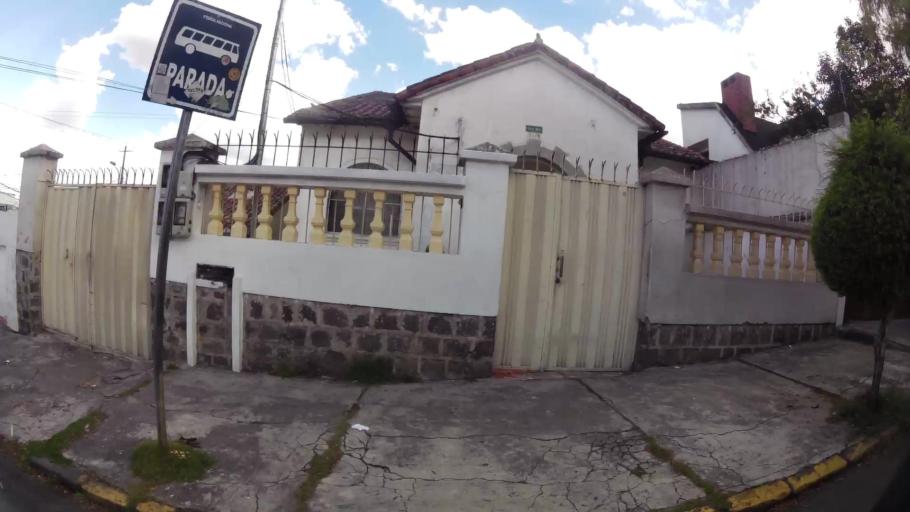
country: EC
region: Pichincha
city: Quito
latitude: -0.1895
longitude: -78.5017
